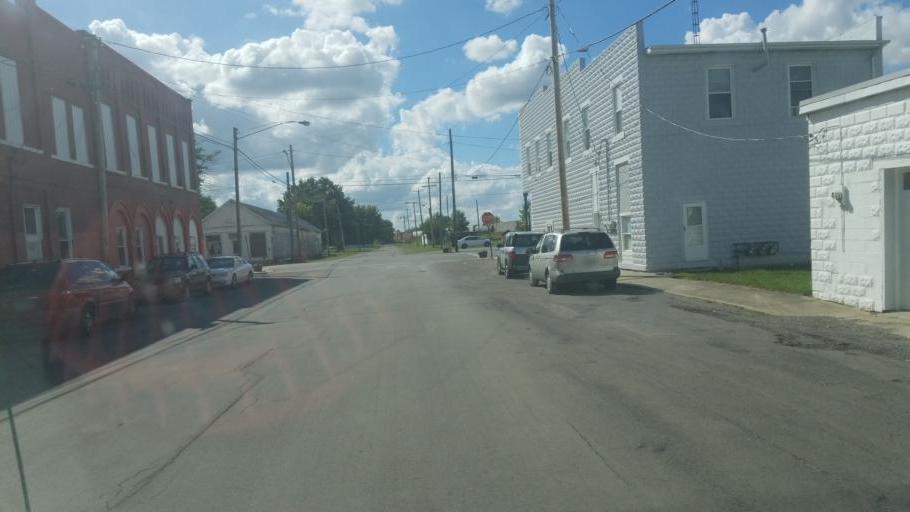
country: US
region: Ohio
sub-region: Hardin County
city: Kenton
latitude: 40.5153
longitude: -83.5727
